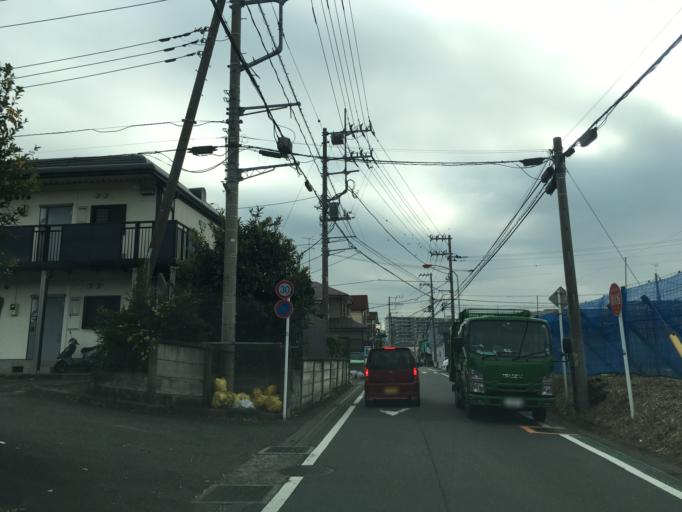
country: JP
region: Kanagawa
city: Minami-rinkan
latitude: 35.5080
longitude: 139.4638
